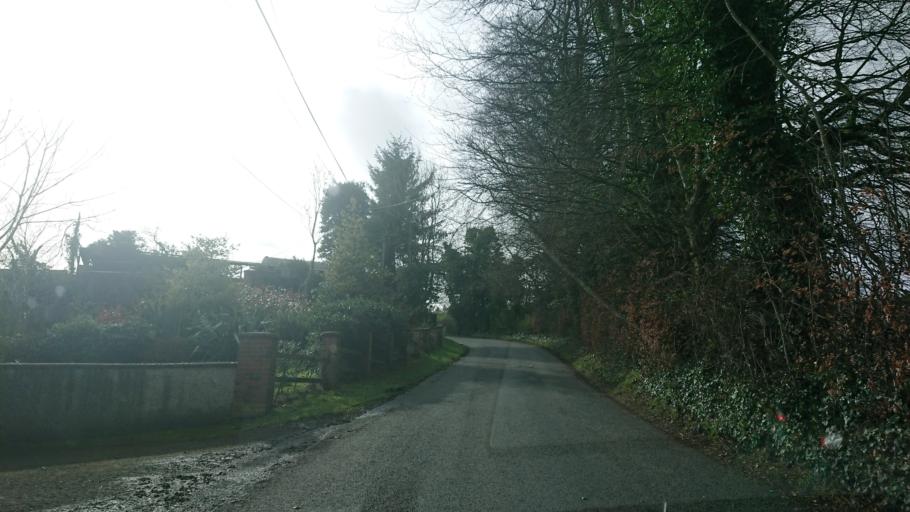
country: IE
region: Leinster
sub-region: Wicklow
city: Blessington
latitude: 53.1567
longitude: -6.5628
